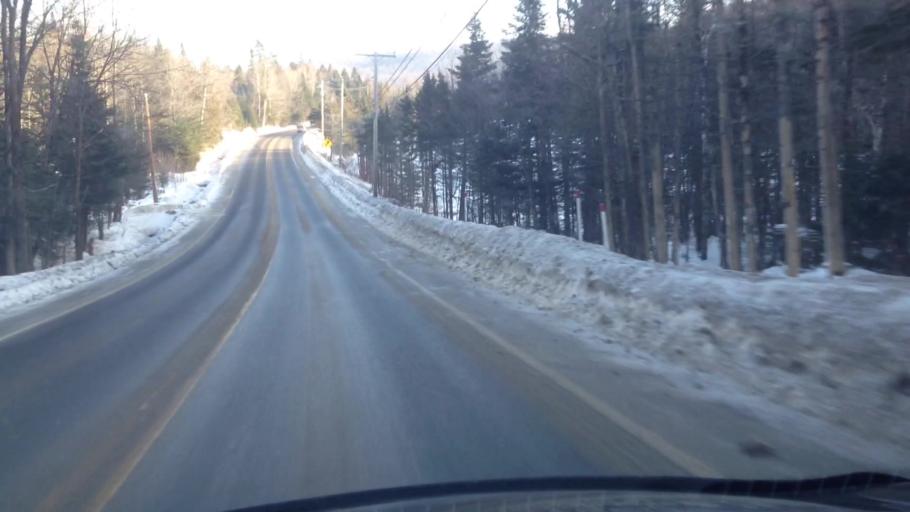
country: CA
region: Quebec
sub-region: Laurentides
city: Sainte-Agathe-des-Monts
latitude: 45.9081
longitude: -74.3293
